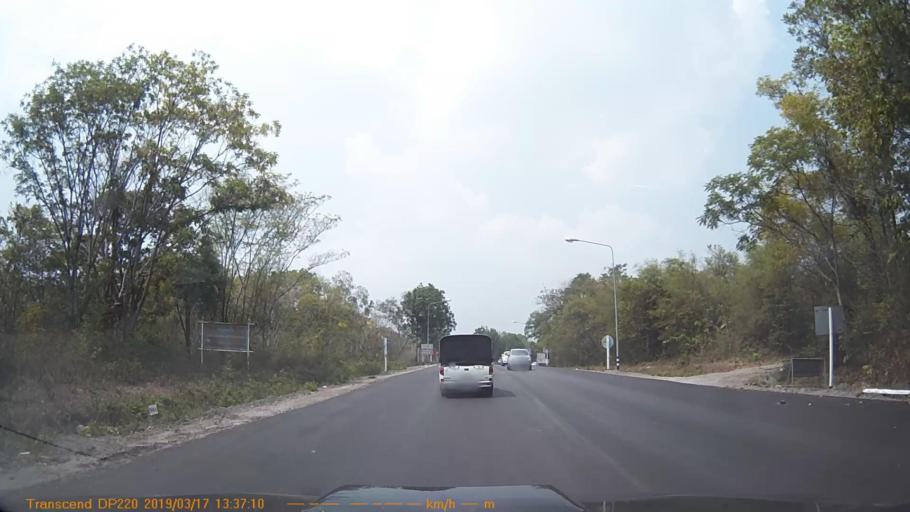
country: TH
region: Buriram
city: Non Din Daeng
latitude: 14.1536
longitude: 102.6613
